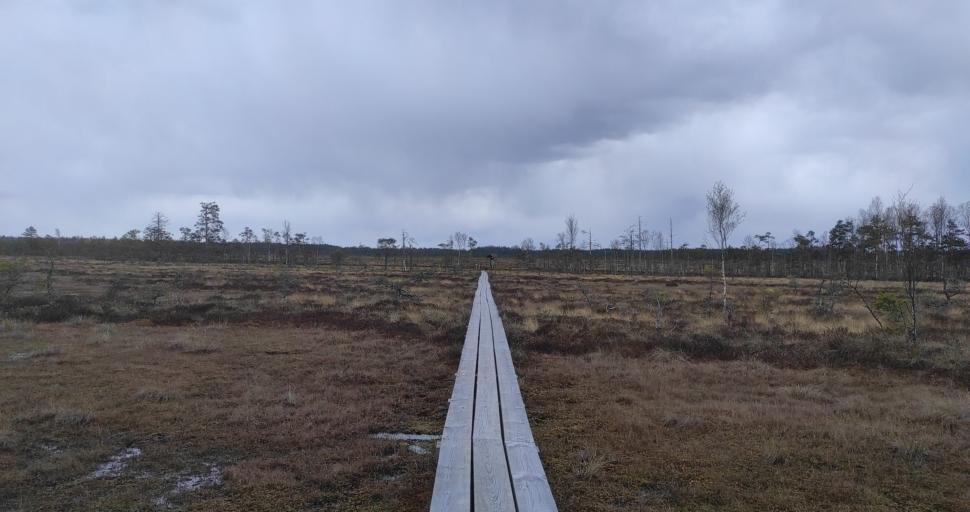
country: LV
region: Dundaga
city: Dundaga
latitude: 57.3453
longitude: 22.1566
